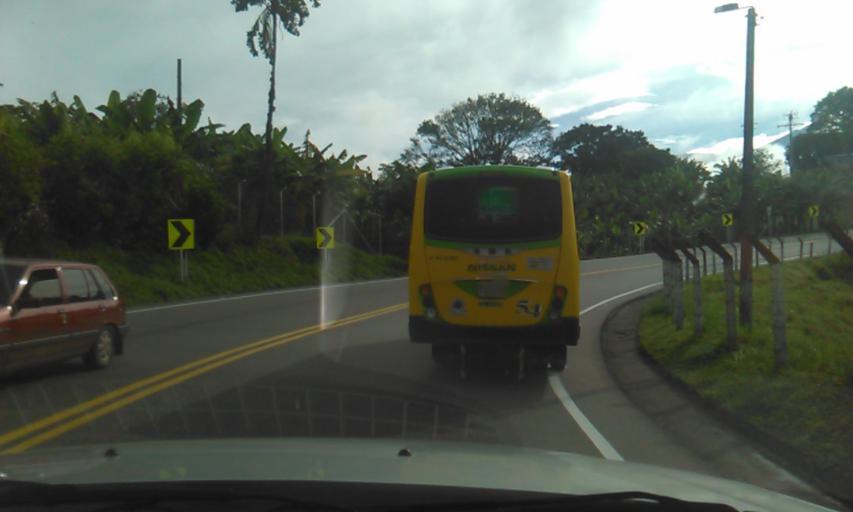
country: CO
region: Quindio
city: Armenia
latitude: 4.4838
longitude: -75.6989
